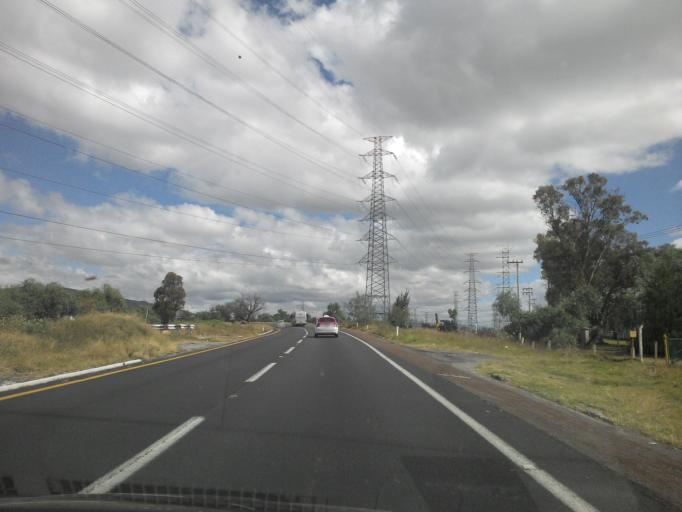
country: MX
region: Morelos
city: Xometla
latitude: 19.6593
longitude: -98.8741
